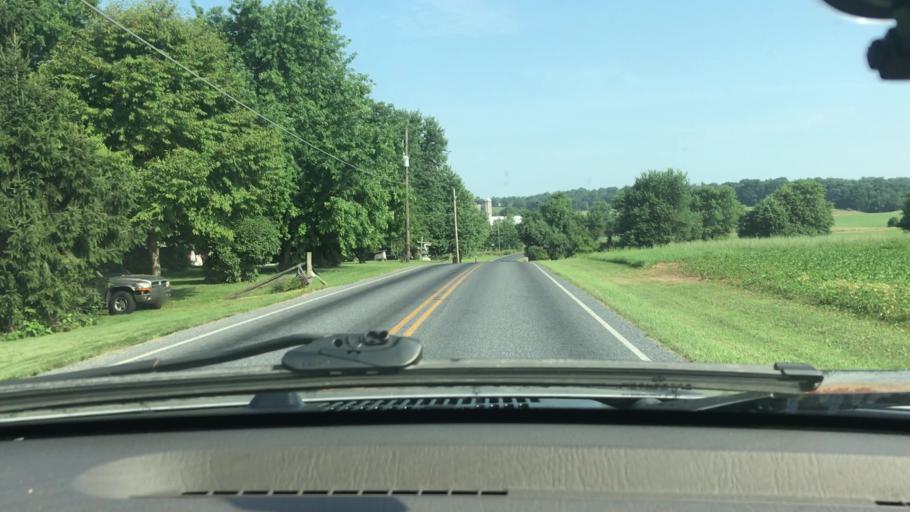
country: US
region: Pennsylvania
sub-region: Lancaster County
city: Elizabethtown
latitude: 40.1652
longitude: -76.5807
